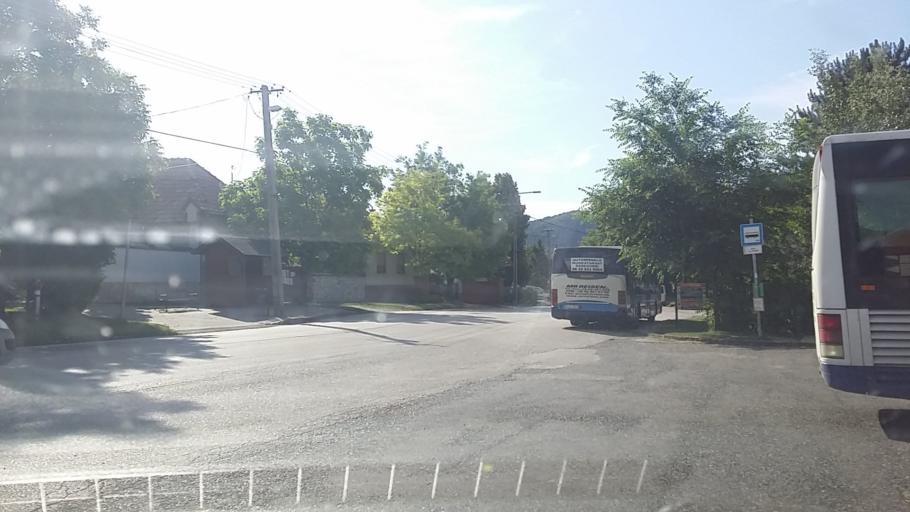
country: HU
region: Komarom-Esztergom
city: Bajna
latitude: 47.6544
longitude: 18.6000
